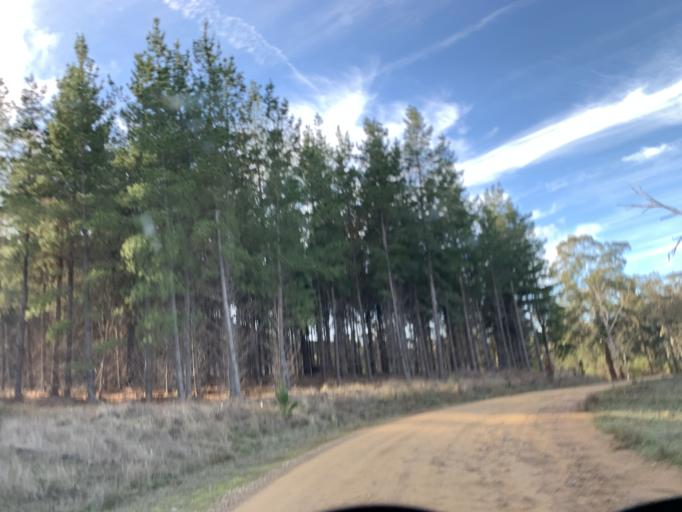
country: AU
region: Victoria
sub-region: Mansfield
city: Mansfield
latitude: -36.9329
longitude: 146.0924
